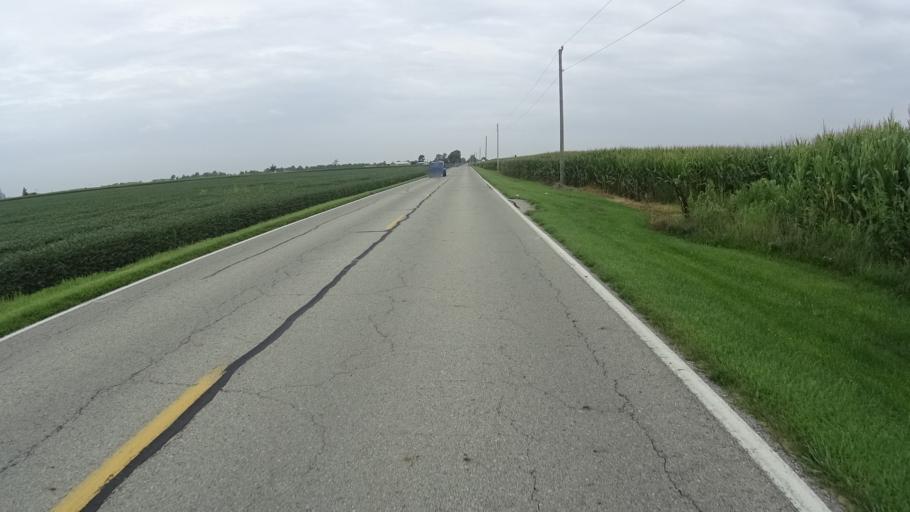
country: US
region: Indiana
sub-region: Madison County
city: Lapel
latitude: 40.0496
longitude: -85.8199
